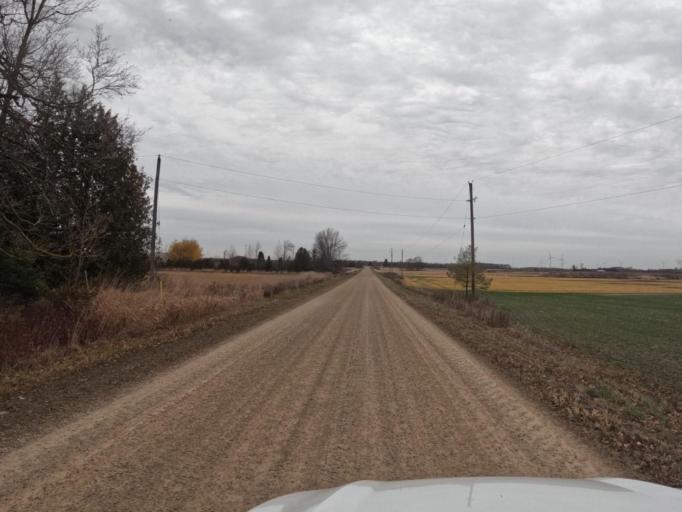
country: CA
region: Ontario
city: Shelburne
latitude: 44.0315
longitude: -80.3714
